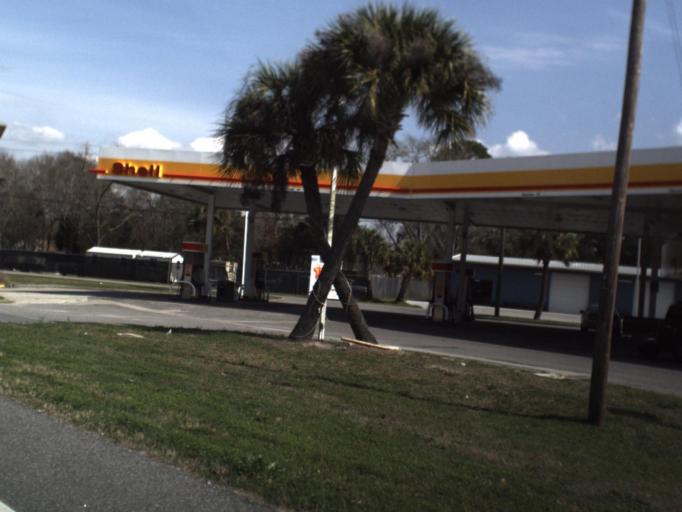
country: US
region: Florida
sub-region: Bay County
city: Lynn Haven
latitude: 30.2297
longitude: -85.6566
